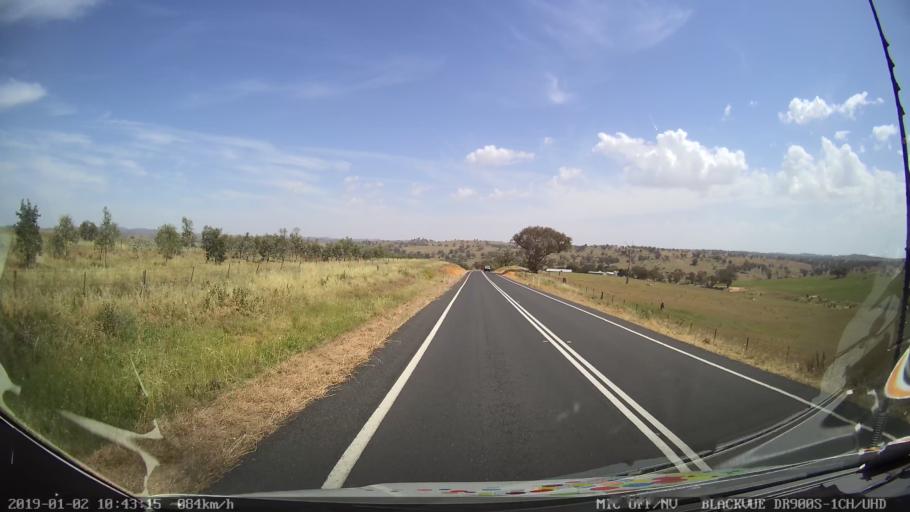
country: AU
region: New South Wales
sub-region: Cootamundra
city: Cootamundra
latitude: -34.7746
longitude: 148.3051
